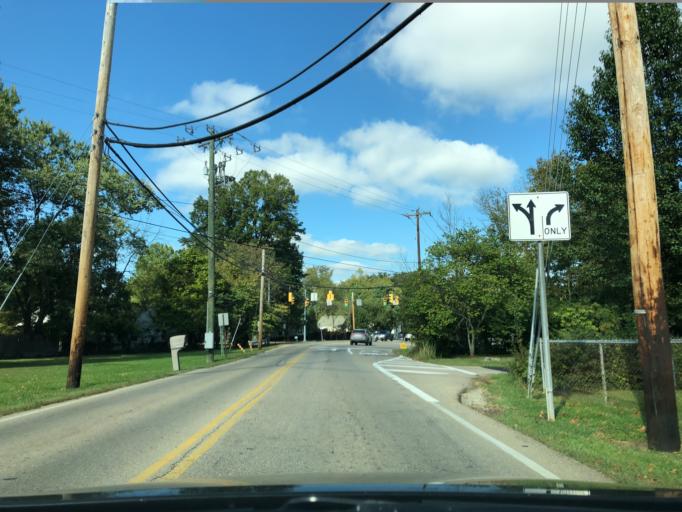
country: US
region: Ohio
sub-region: Hamilton County
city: Loveland
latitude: 39.2580
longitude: -84.2497
